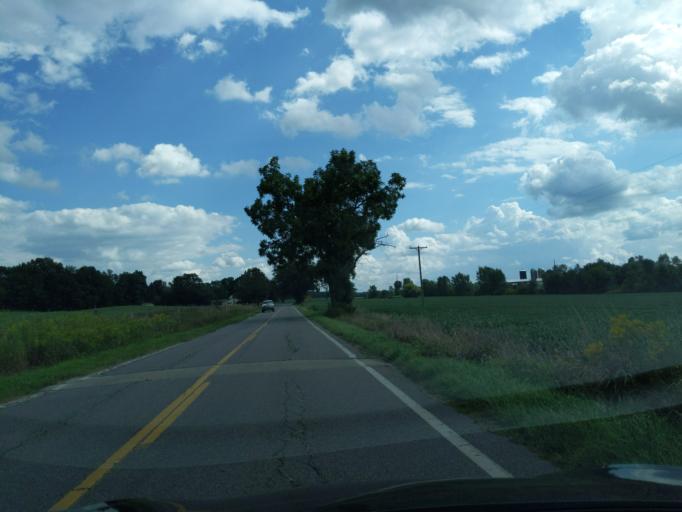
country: US
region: Michigan
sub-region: Jackson County
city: Spring Arbor
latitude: 42.3340
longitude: -84.5445
